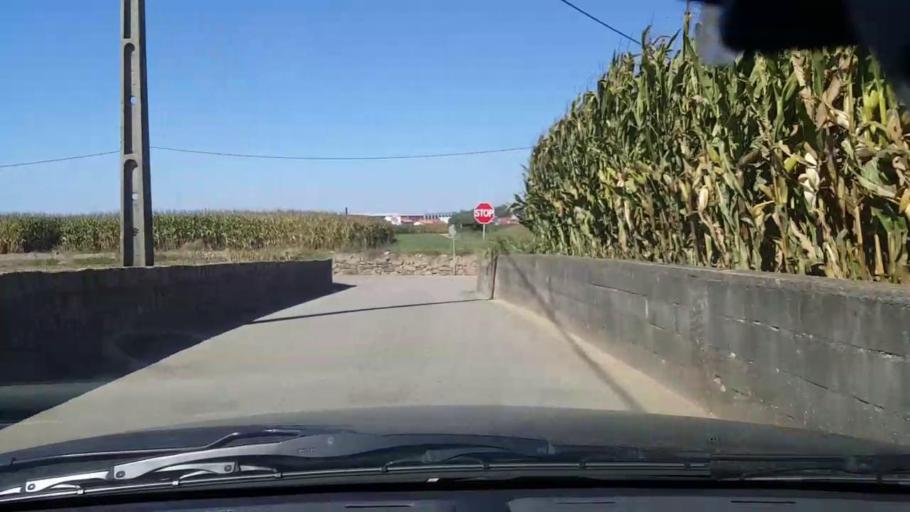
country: PT
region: Porto
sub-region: Matosinhos
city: Lavra
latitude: 41.2917
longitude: -8.6942
